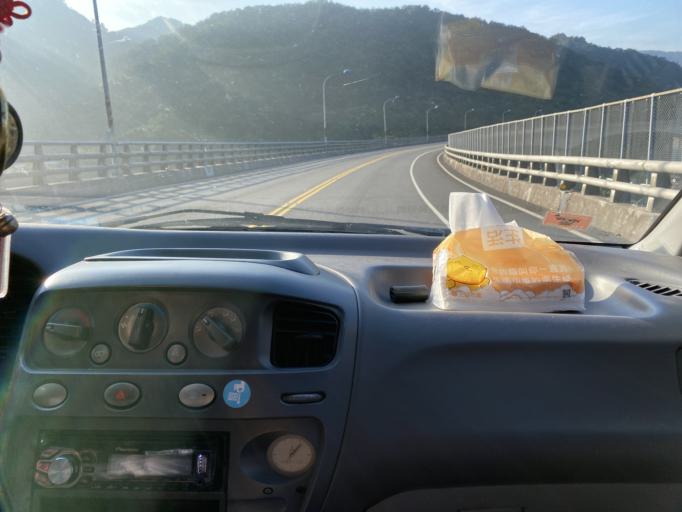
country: TW
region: Taiwan
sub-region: Keelung
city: Keelung
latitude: 25.0454
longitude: 121.7799
